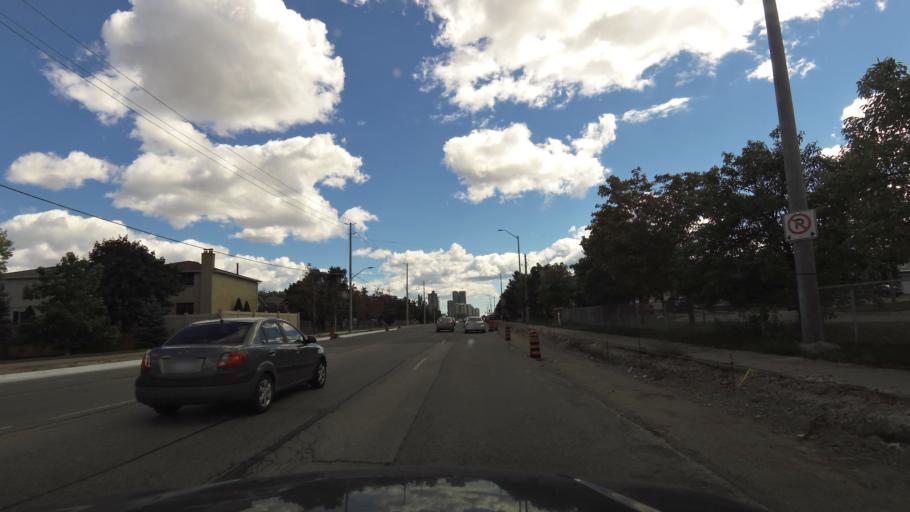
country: CA
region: Ontario
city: Mississauga
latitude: 43.5990
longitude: -79.6662
